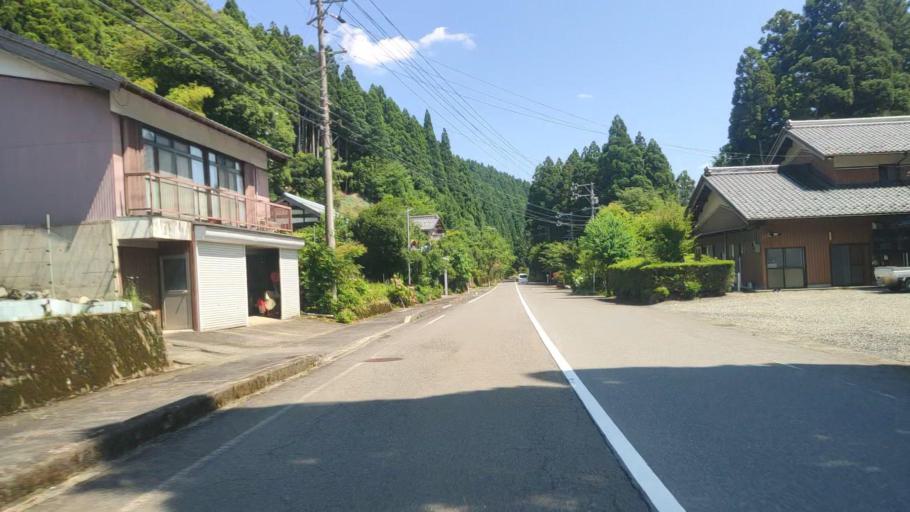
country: JP
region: Gifu
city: Godo
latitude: 35.6460
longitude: 136.6028
